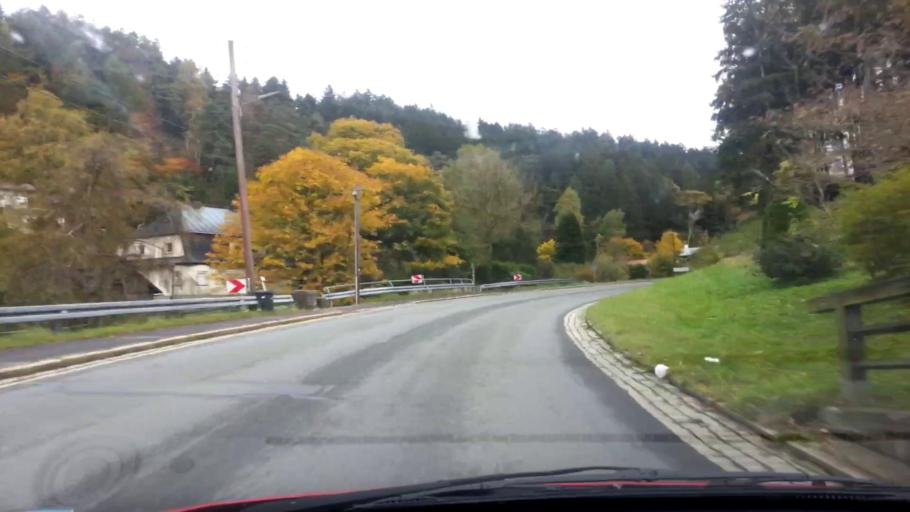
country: DE
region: Bavaria
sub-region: Upper Franconia
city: Warmensteinach
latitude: 50.0013
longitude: 11.7907
